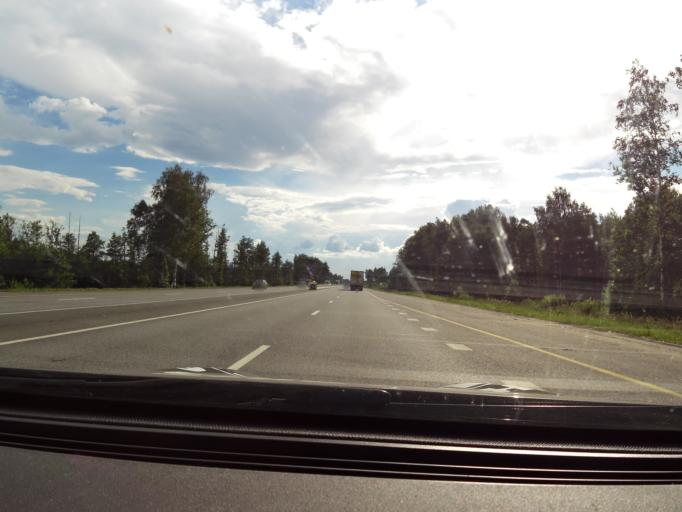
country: RU
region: Vladimir
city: Galitsy
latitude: 56.2417
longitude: 42.8448
